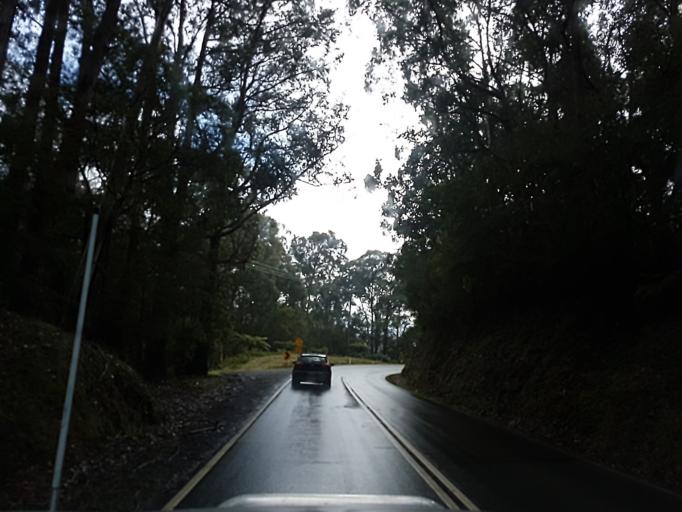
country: AU
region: Victoria
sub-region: Yarra Ranges
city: Millgrove
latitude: -37.7329
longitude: 145.7447
